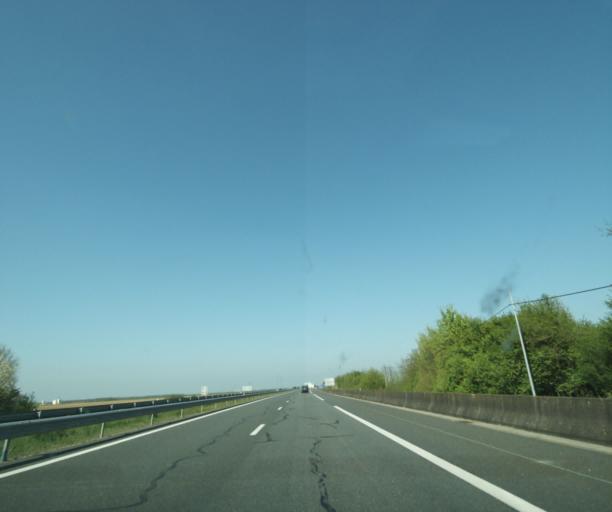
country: FR
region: Centre
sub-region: Departement du Loiret
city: Corquilleroy
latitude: 48.0653
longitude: 2.6735
